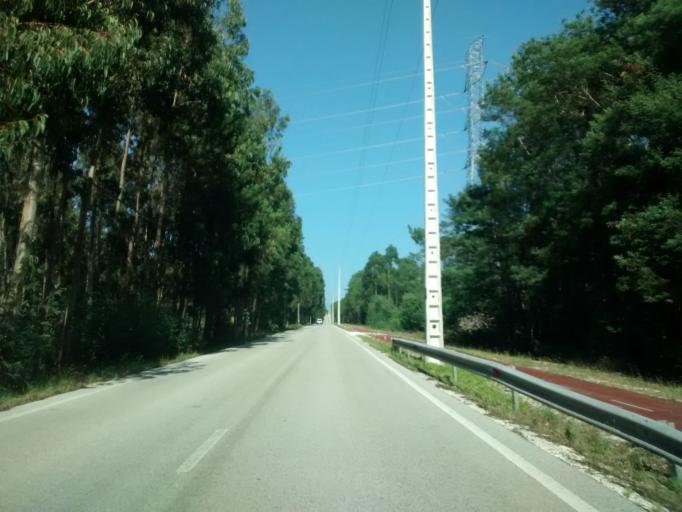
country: PT
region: Leiria
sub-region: Leiria
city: Monte Redondo
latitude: 39.9798
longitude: -8.8276
